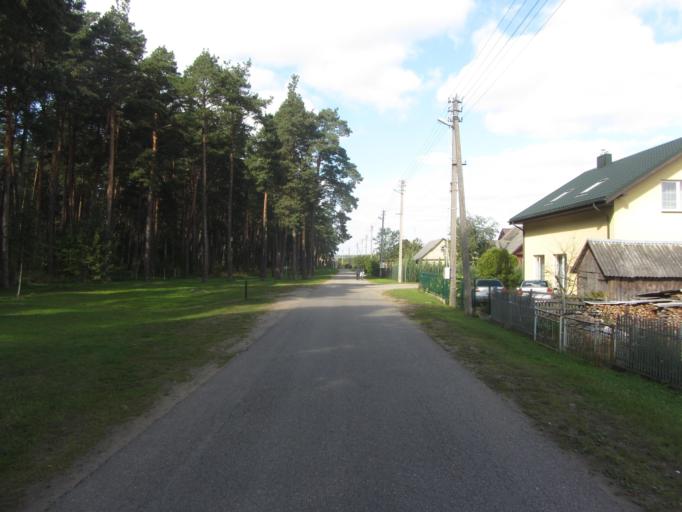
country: LT
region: Vilnius County
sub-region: Trakai
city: Rudiskes
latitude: 54.5174
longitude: 24.8225
